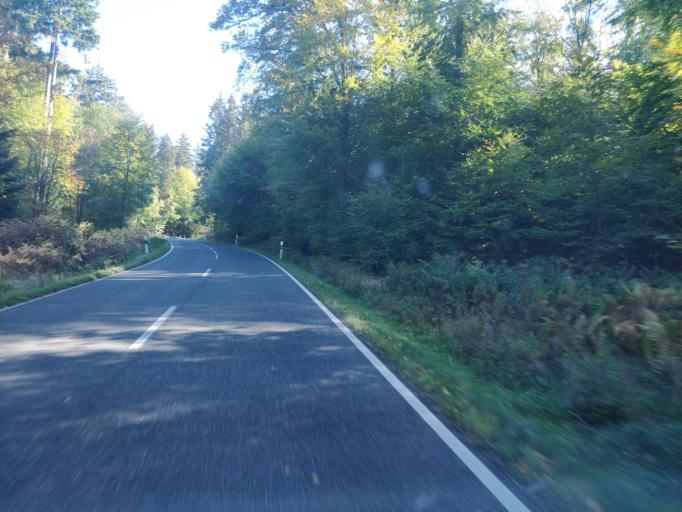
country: DE
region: North Rhine-Westphalia
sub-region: Regierungsbezirk Koln
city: Bad Munstereifel
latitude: 50.5478
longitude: 6.8081
